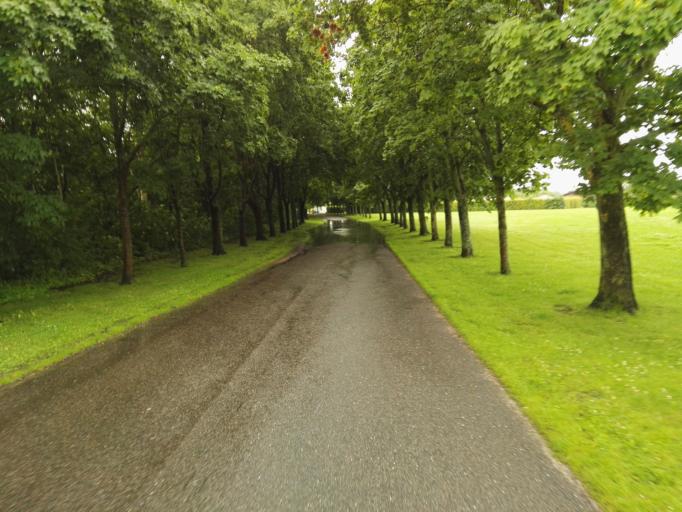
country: DK
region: Capital Region
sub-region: Ballerup Kommune
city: Ballerup
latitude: 55.7148
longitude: 12.3505
